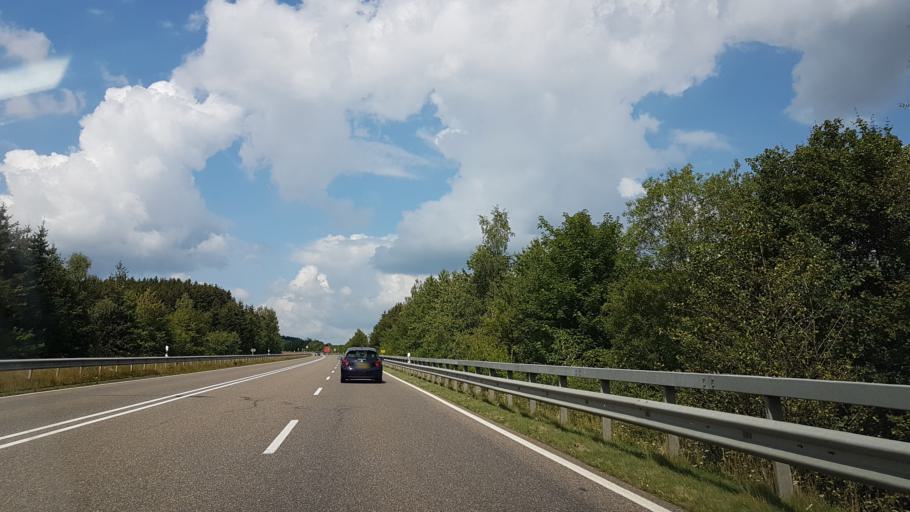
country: DE
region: Rheinland-Pfalz
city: Brandscheid
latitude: 50.2065
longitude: 6.3277
